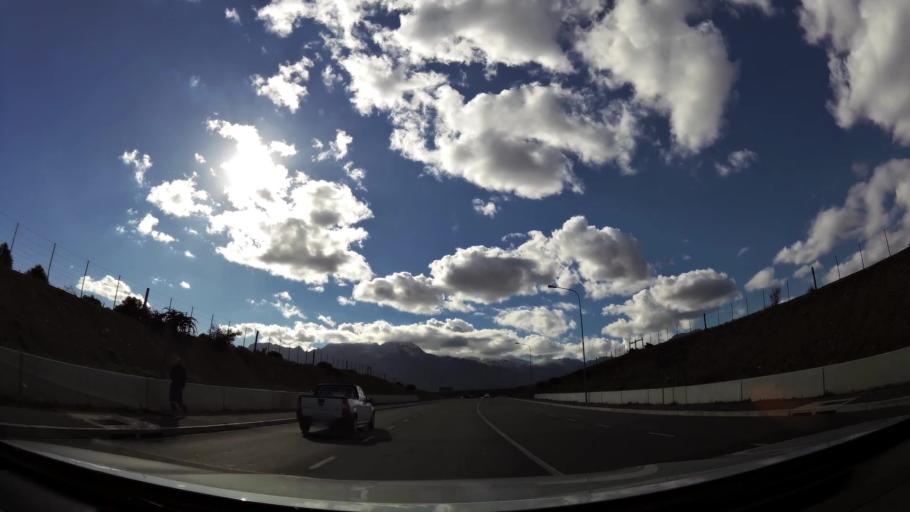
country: ZA
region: Western Cape
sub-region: Cape Winelands District Municipality
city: Worcester
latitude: -33.6336
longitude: 19.4272
